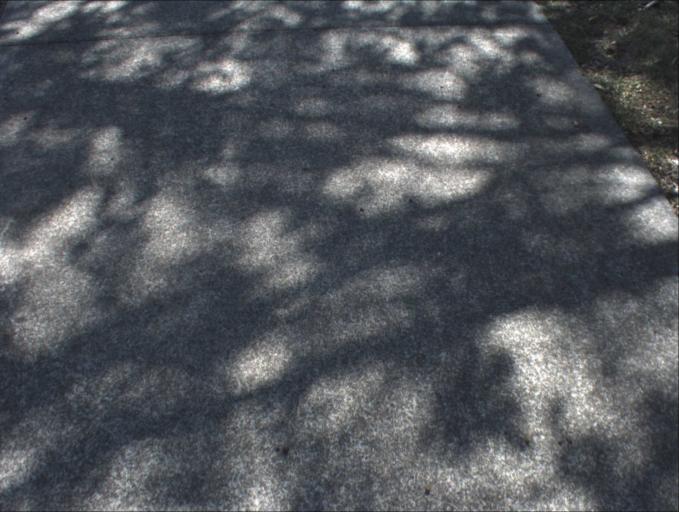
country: AU
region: Queensland
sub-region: Gold Coast
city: Yatala
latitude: -27.7076
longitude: 153.2276
